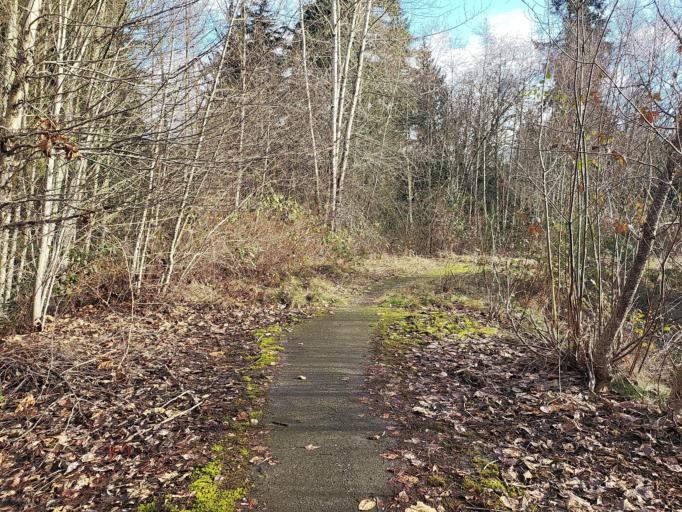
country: US
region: Washington
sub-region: King County
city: Newcastle
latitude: 47.5317
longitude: -122.1297
